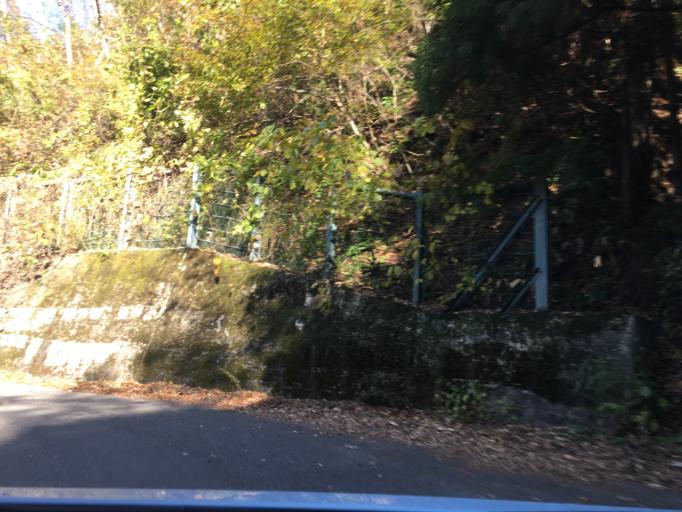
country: JP
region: Fukushima
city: Inawashiro
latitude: 37.4293
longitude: 139.9828
